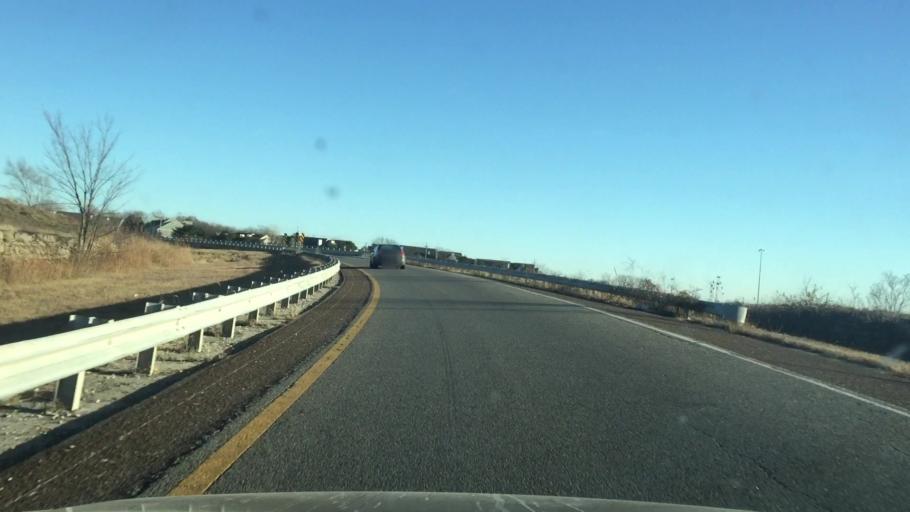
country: US
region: Kansas
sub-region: Wyandotte County
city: Edwardsville
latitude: 39.0093
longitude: -94.7864
